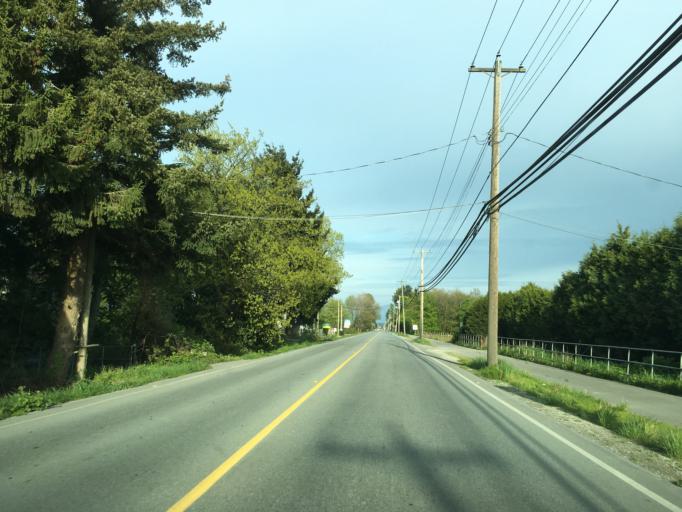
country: CA
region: British Columbia
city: Richmond
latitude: 49.1699
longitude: -123.0623
